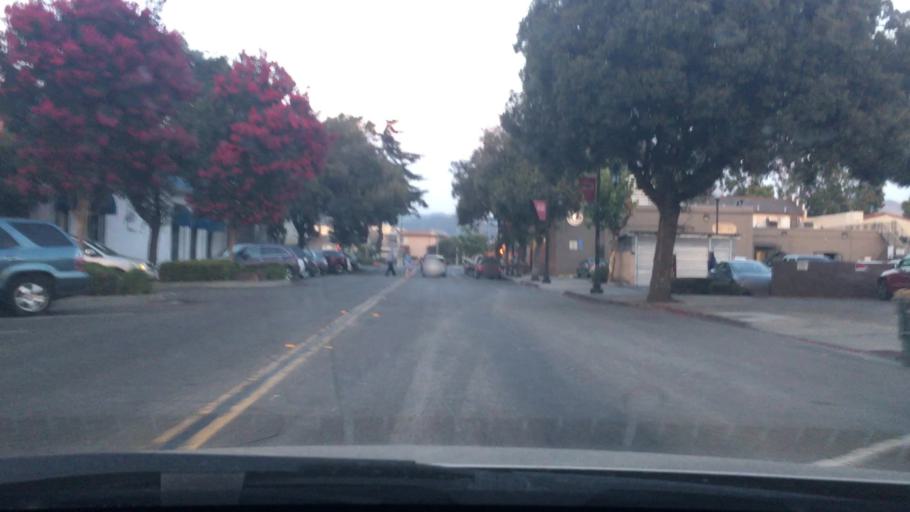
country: US
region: California
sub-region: Alameda County
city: San Leandro
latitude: 37.7231
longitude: -122.1549
